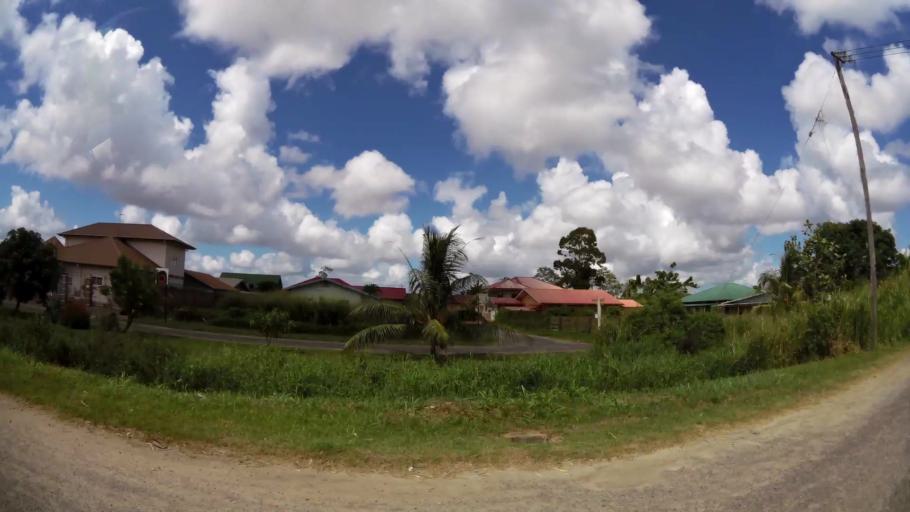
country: SR
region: Paramaribo
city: Paramaribo
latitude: 5.8665
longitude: -55.1324
